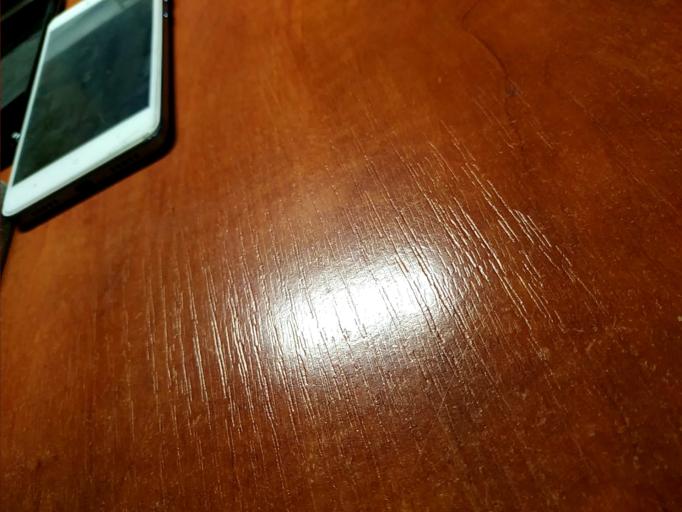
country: RU
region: Kaluga
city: Iznoski
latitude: 54.9721
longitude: 35.4137
